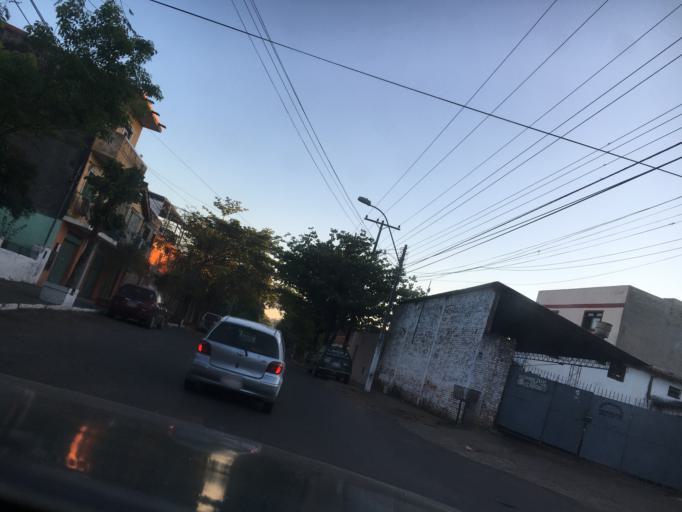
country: PY
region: Central
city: Lambare
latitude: -25.3212
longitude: -57.6107
